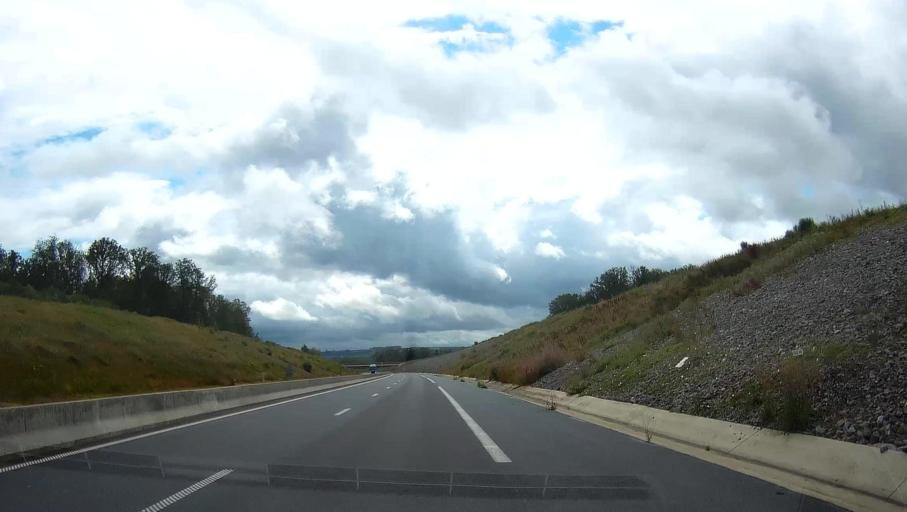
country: FR
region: Champagne-Ardenne
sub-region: Departement des Ardennes
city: Rimogne
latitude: 49.8277
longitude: 4.5116
